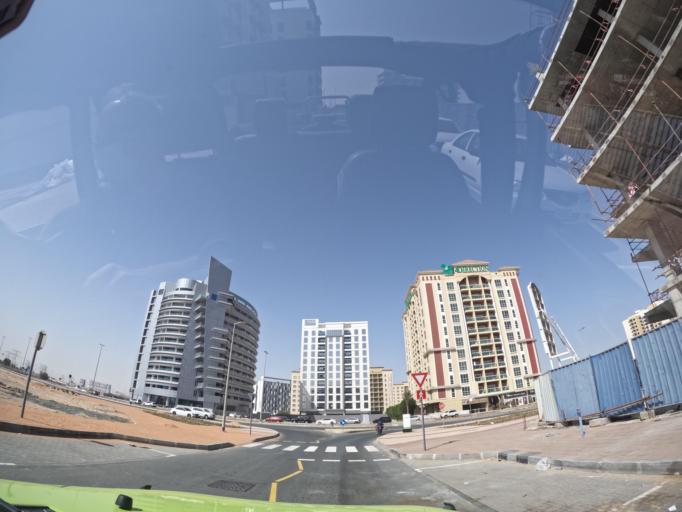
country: AE
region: Dubai
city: Dubai
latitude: 25.0859
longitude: 55.3865
